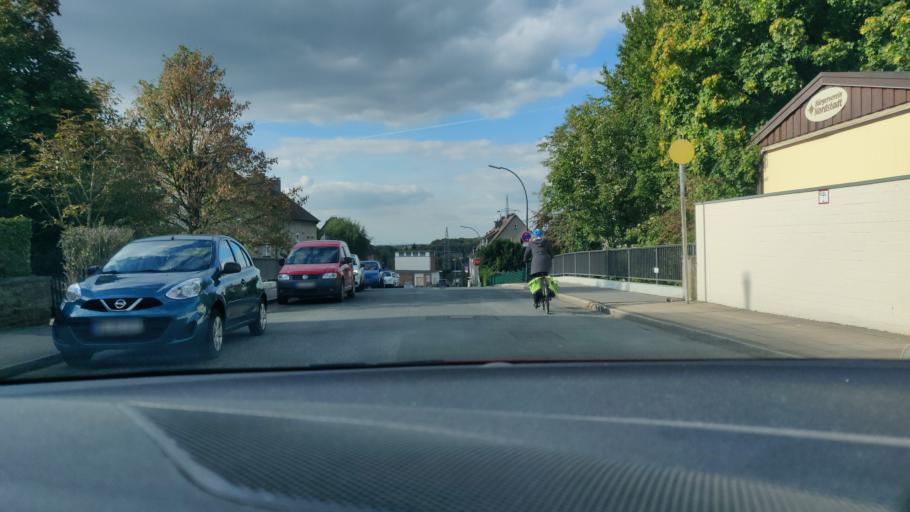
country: DE
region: North Rhine-Westphalia
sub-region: Regierungsbezirk Dusseldorf
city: Velbert
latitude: 51.3468
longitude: 7.0424
